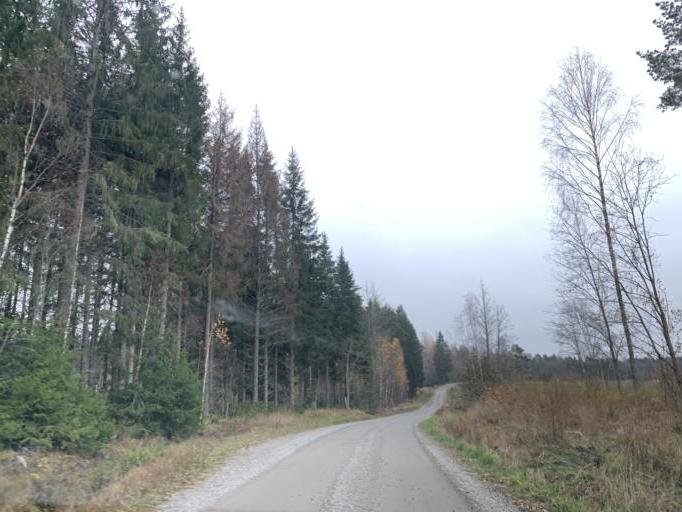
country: SE
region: Vaestmanland
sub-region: Surahammars Kommun
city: Ramnas
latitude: 59.7089
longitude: 16.0916
